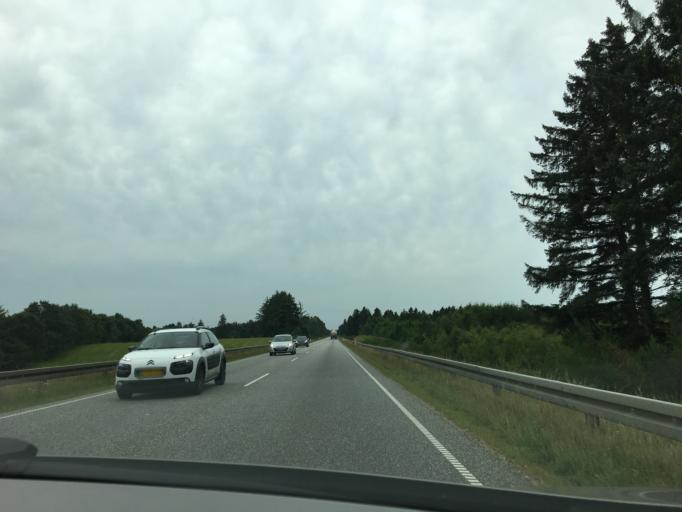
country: DK
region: Central Jutland
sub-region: Herning Kommune
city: Sunds
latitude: 56.3691
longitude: 8.9810
